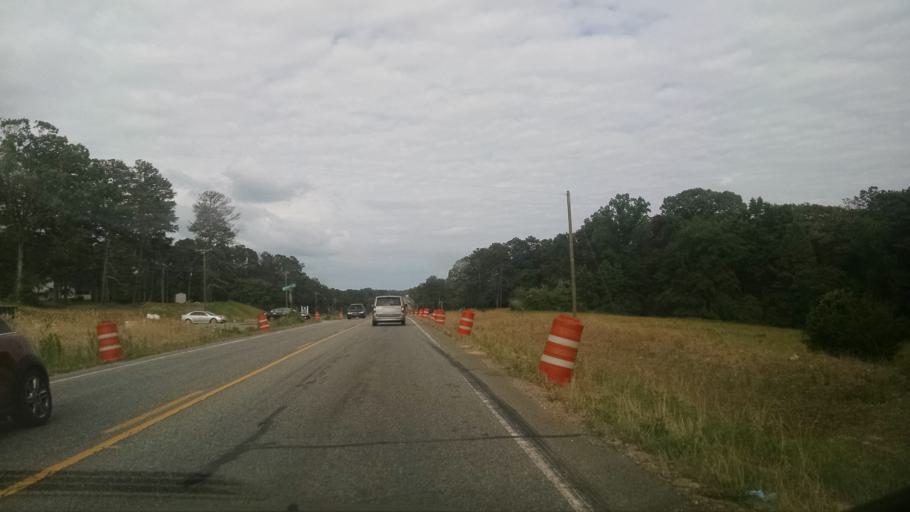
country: US
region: Georgia
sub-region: Gwinnett County
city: Sugar Hill
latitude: 34.1120
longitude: -84.0639
